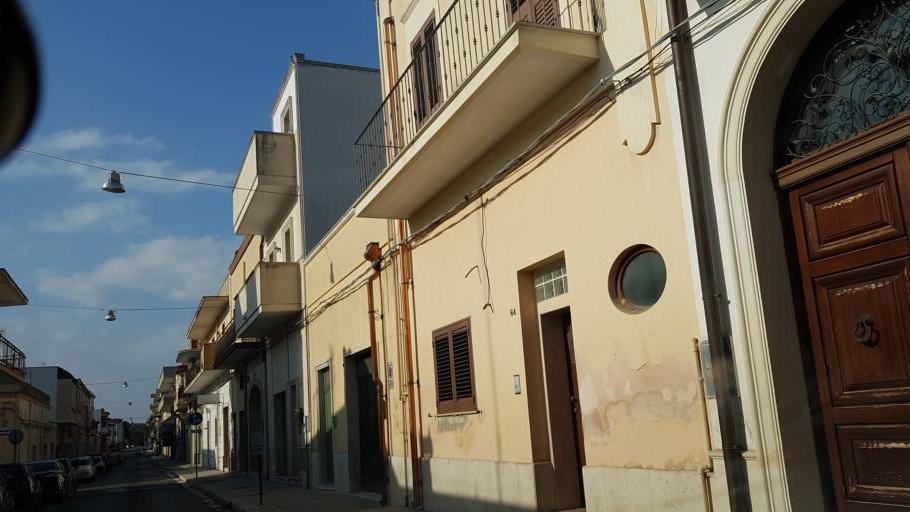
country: IT
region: Apulia
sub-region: Provincia di Brindisi
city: Mesagne
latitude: 40.5624
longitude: 17.8061
